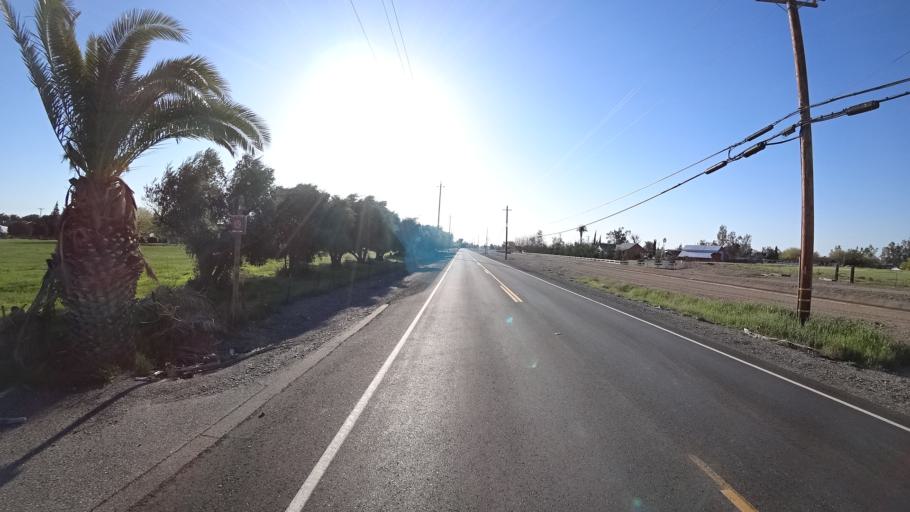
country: US
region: California
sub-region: Glenn County
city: Orland
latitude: 39.7611
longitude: -122.2315
